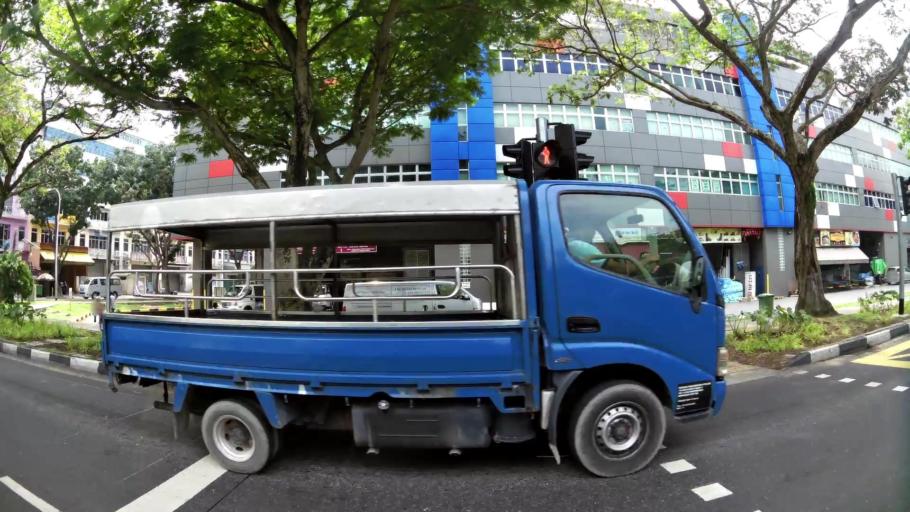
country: SG
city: Singapore
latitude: 1.3375
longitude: 103.9033
